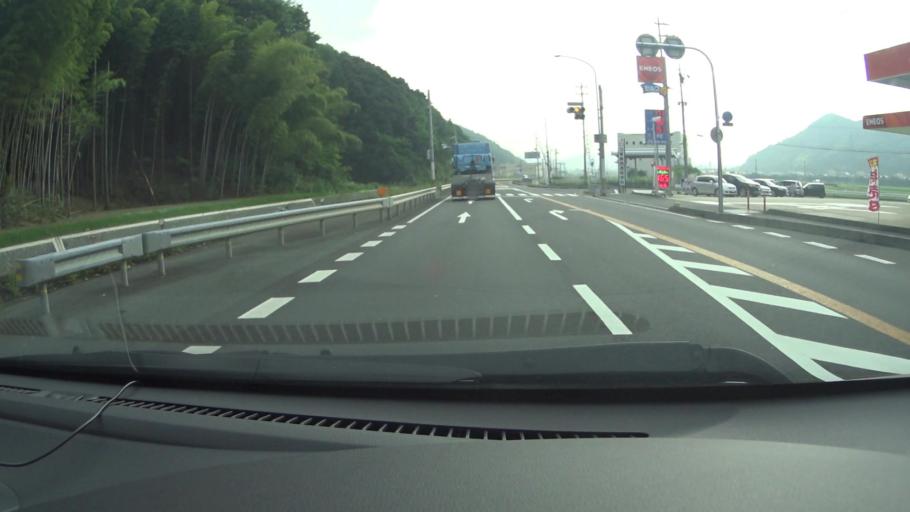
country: JP
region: Kyoto
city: Maizuru
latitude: 35.4803
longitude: 135.4148
